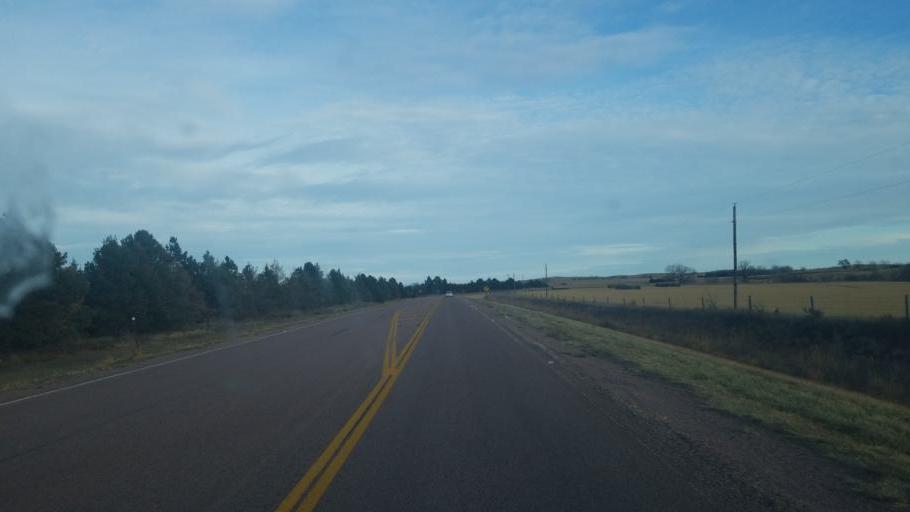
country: US
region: South Dakota
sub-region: Bon Homme County
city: Springfield
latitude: 42.7332
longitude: -97.8859
